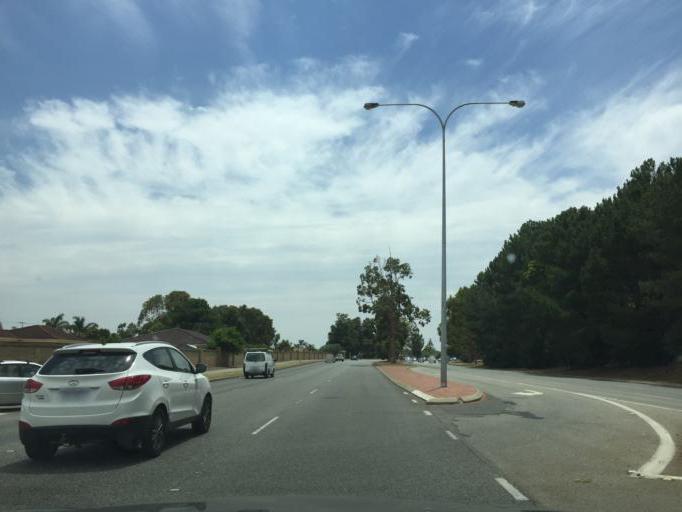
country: AU
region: Western Australia
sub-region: Melville
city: Winthrop
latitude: -32.0659
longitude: 115.8292
